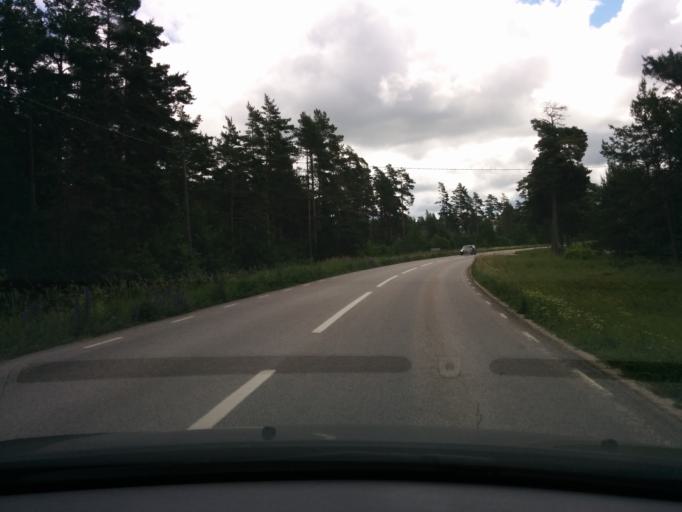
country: SE
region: Gotland
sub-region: Gotland
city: Visby
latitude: 57.6343
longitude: 18.5474
